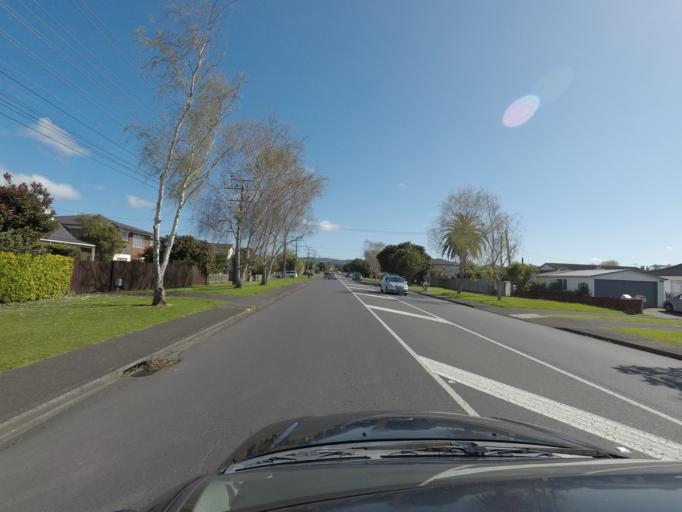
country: NZ
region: Auckland
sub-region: Auckland
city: Rosebank
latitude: -36.8621
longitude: 174.6081
